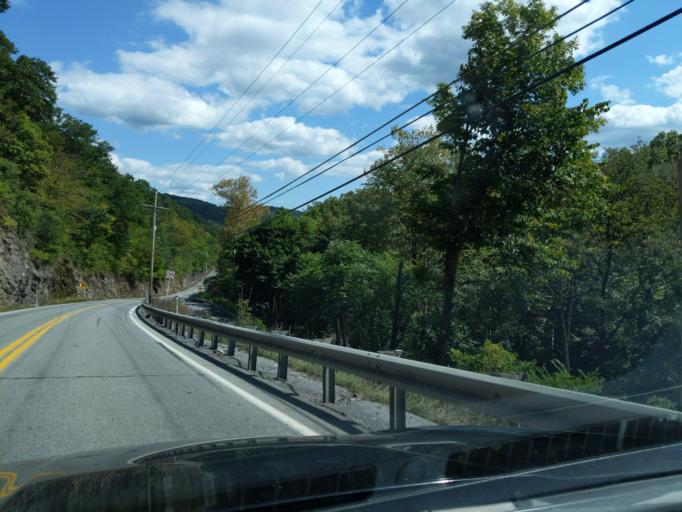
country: US
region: Pennsylvania
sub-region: Blair County
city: Tyrone
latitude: 40.6577
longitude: -78.2107
